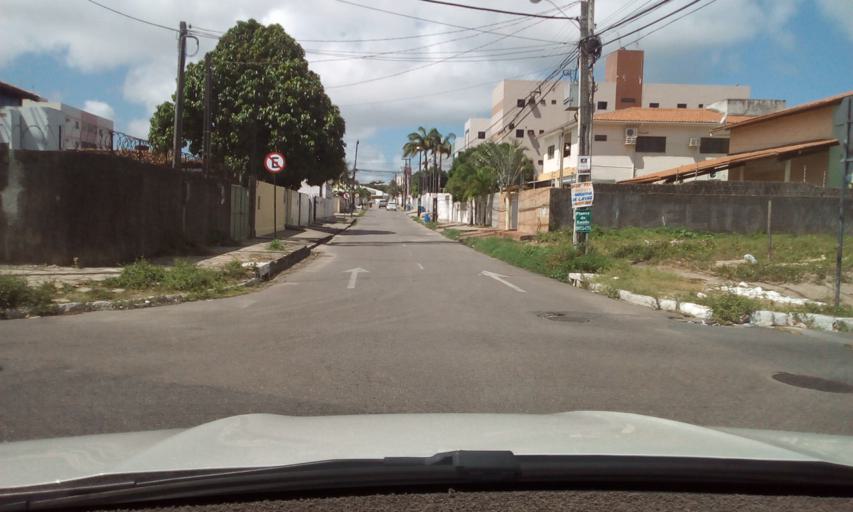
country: BR
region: Paraiba
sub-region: Joao Pessoa
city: Joao Pessoa
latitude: -7.1562
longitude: -34.8359
